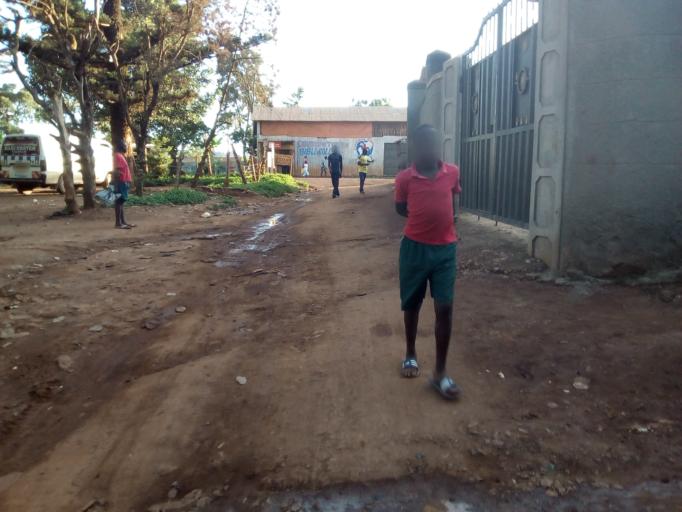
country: UG
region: Central Region
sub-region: Wakiso District
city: Kajansi
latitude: 0.2475
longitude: 32.5750
